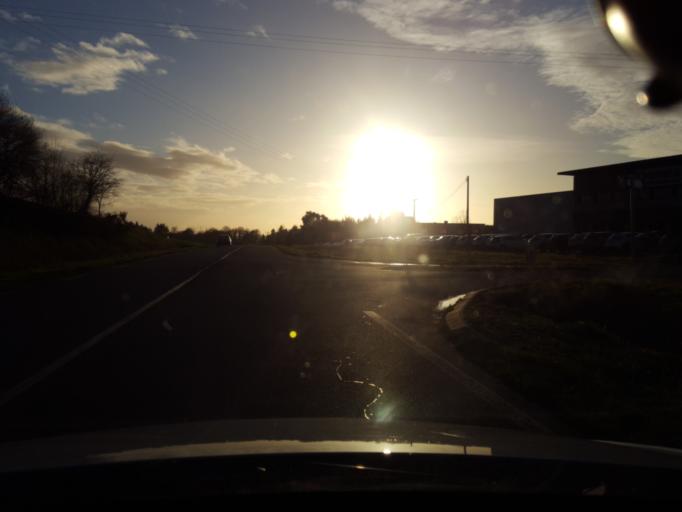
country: FR
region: Brittany
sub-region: Departement d'Ille-et-Vilaine
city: Guignen
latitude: 47.9331
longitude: -1.8472
